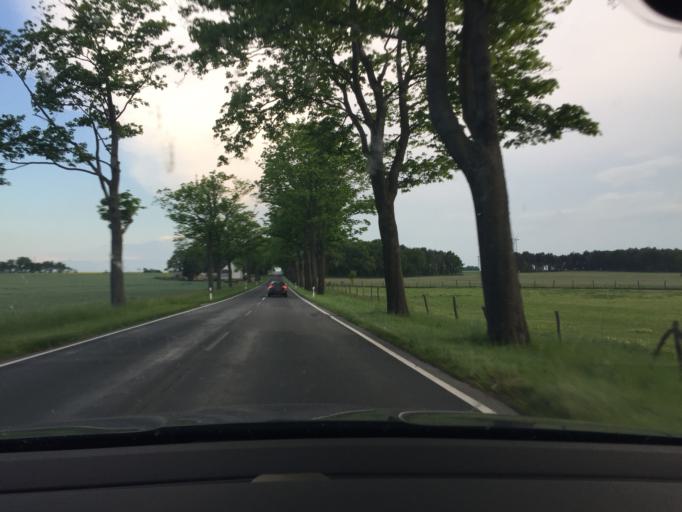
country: DE
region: Saxony-Anhalt
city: Kropstadt
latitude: 52.0324
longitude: 12.8032
